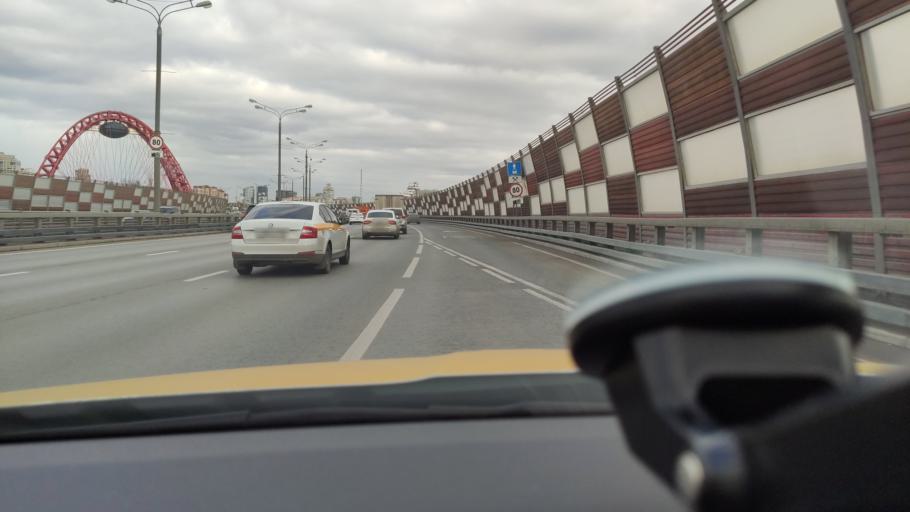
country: RU
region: Moscow
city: Shchukino
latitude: 55.7723
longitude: 37.4358
